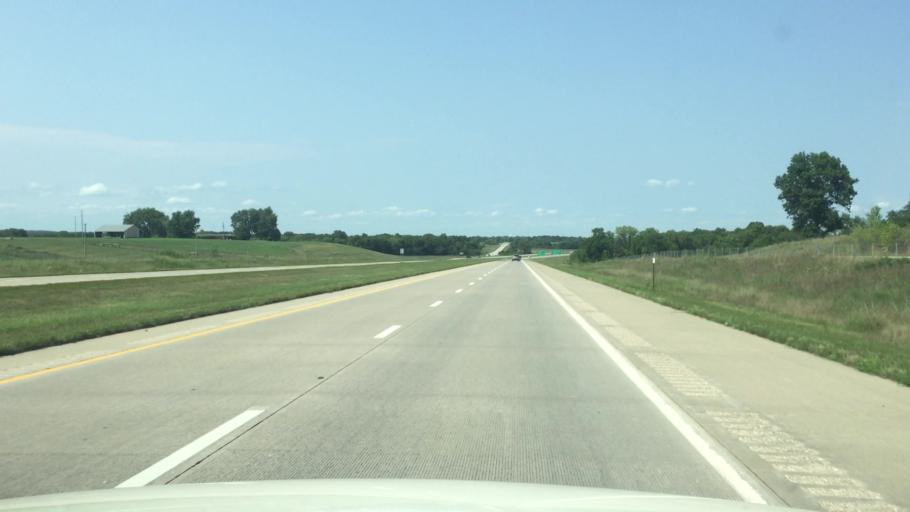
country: US
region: Kansas
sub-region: Linn County
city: Pleasanton
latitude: 38.1290
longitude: -94.7133
